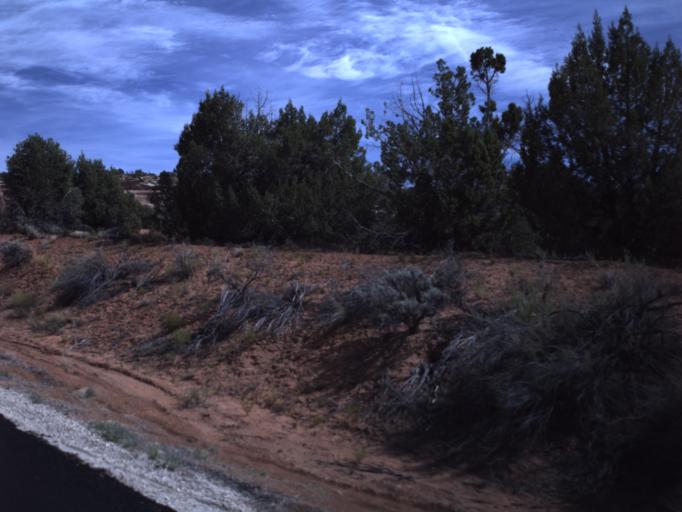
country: US
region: Utah
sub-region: San Juan County
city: Blanding
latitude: 37.5372
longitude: -109.6194
